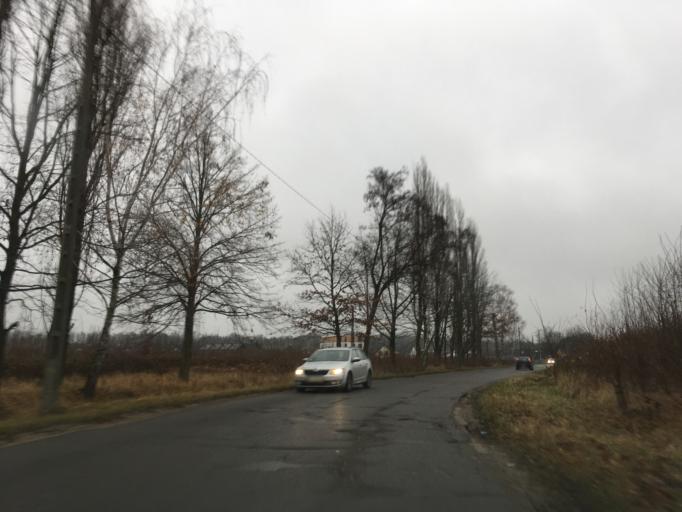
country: PL
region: Masovian Voivodeship
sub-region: Powiat piaseczynski
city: Lesznowola
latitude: 52.0707
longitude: 20.8903
